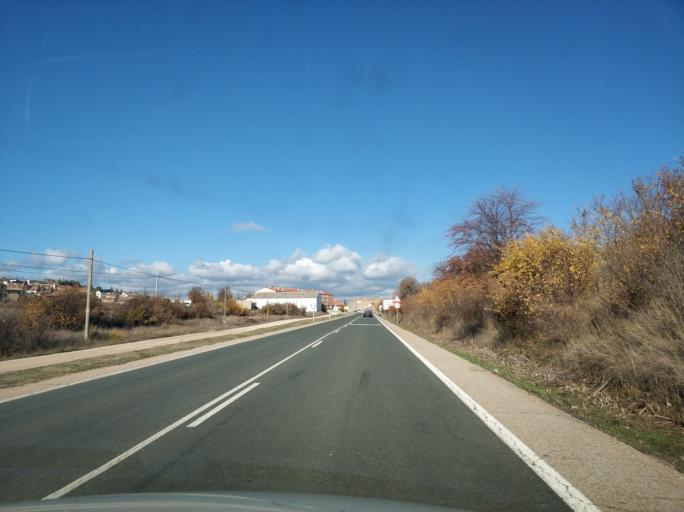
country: ES
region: Castille and Leon
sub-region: Provincia de Soria
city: Almazan
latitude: 41.4768
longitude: -2.5298
